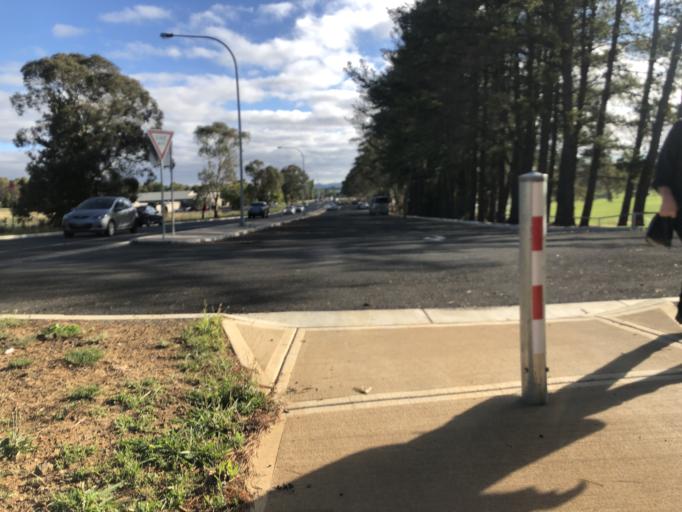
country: AU
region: New South Wales
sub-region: Orange Municipality
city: Orange
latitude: -33.3099
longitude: 149.0963
